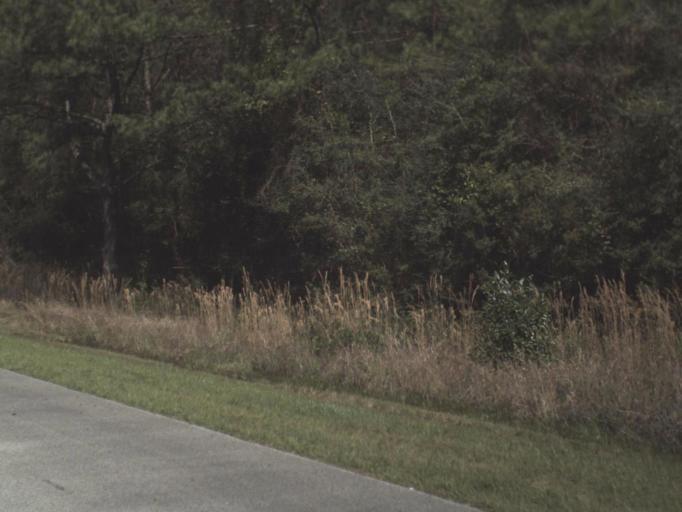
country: US
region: Florida
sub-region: Walton County
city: DeFuniak Springs
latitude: 30.7233
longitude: -86.1925
